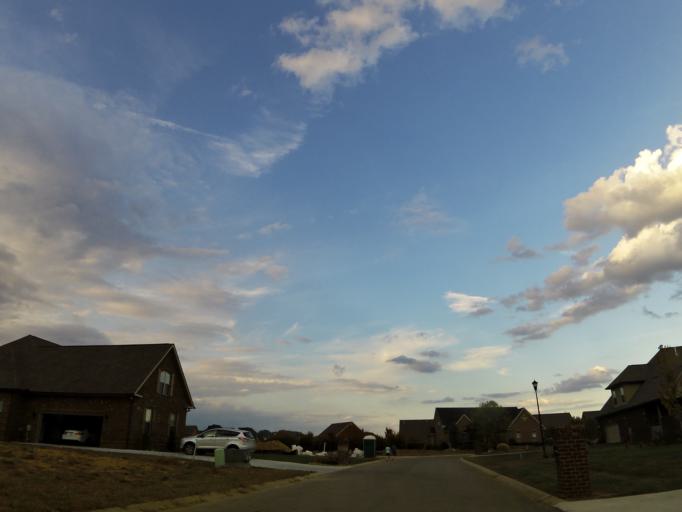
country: US
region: Tennessee
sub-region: Blount County
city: Maryville
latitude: 35.7641
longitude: -84.0273
